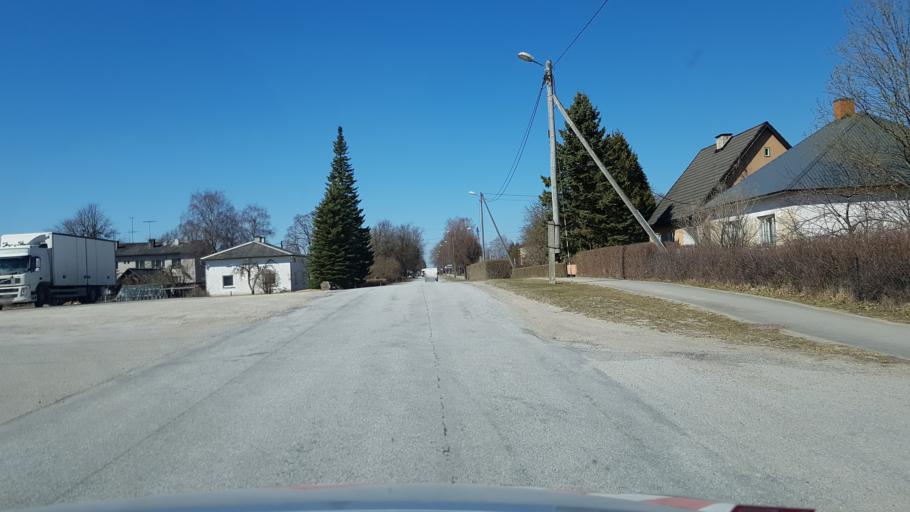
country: EE
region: Laeaene-Virumaa
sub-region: Rakke vald
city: Rakke
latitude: 58.9900
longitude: 26.2350
